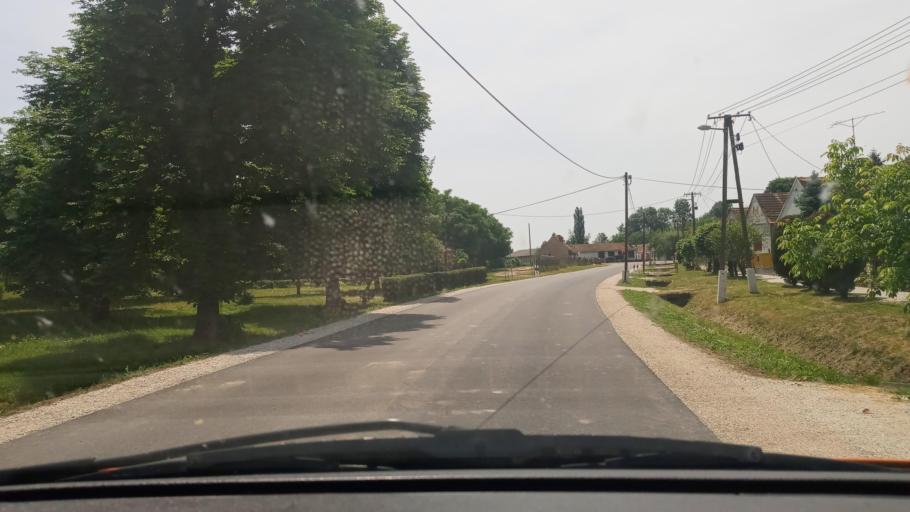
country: HU
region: Baranya
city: Szigetvar
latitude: 45.9614
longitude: 17.6589
